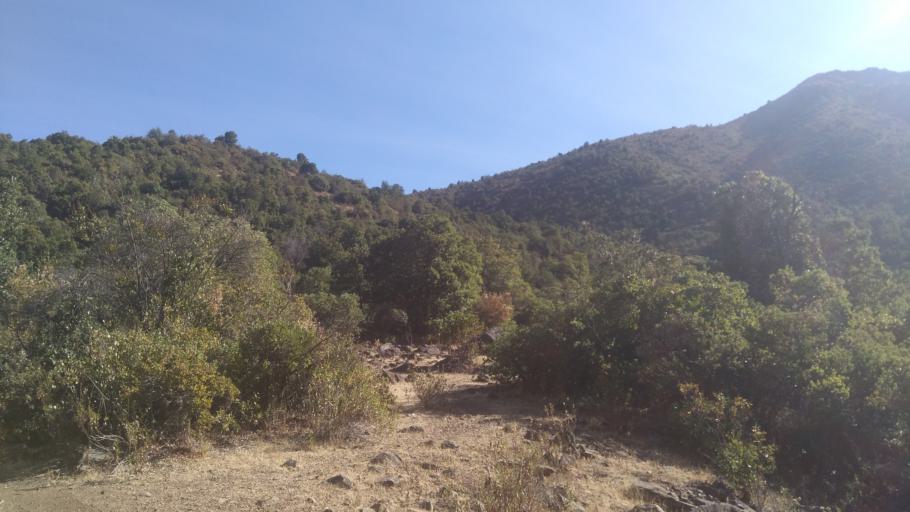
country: CL
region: Santiago Metropolitan
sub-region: Provincia de Cordillera
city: Puente Alto
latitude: -33.7171
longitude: -70.4623
